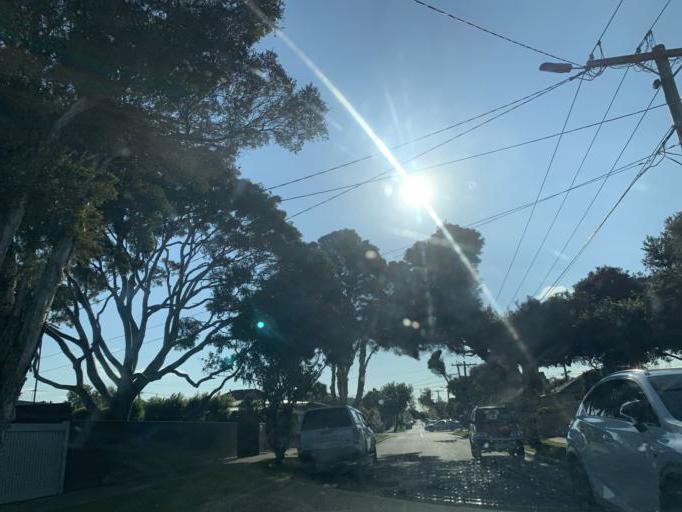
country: AU
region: Victoria
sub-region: Kingston
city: Mordialloc
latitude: -37.9975
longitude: 145.0928
